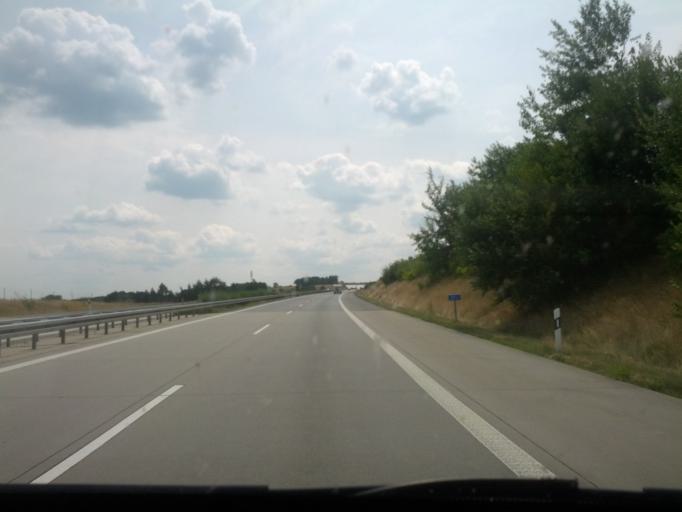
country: DE
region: Saxony
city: Dohna
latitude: 50.9284
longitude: 13.8897
